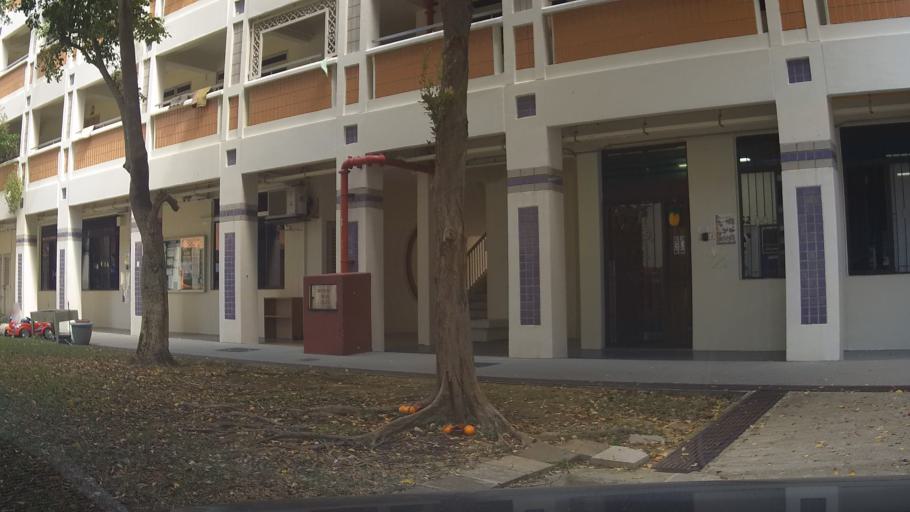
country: SG
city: Singapore
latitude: 1.3669
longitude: 103.9522
